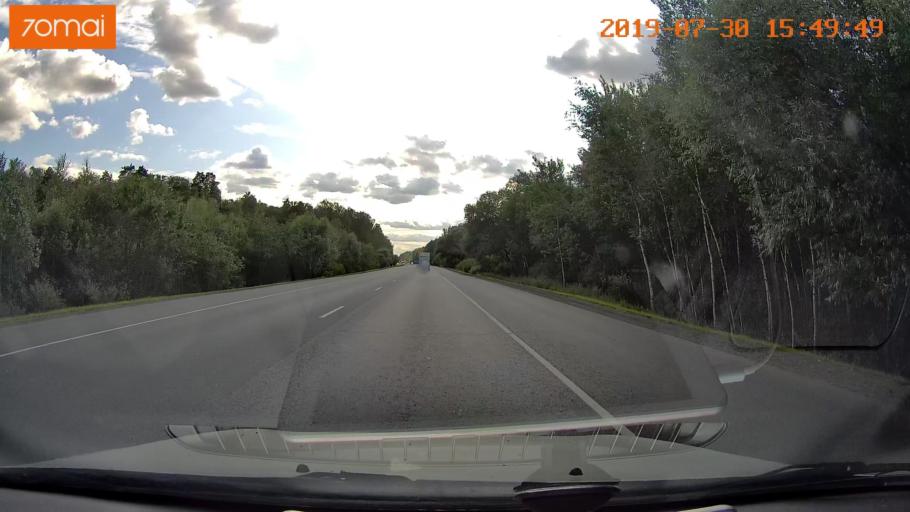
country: RU
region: Moskovskaya
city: Voskresensk
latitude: 55.3354
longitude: 38.6611
